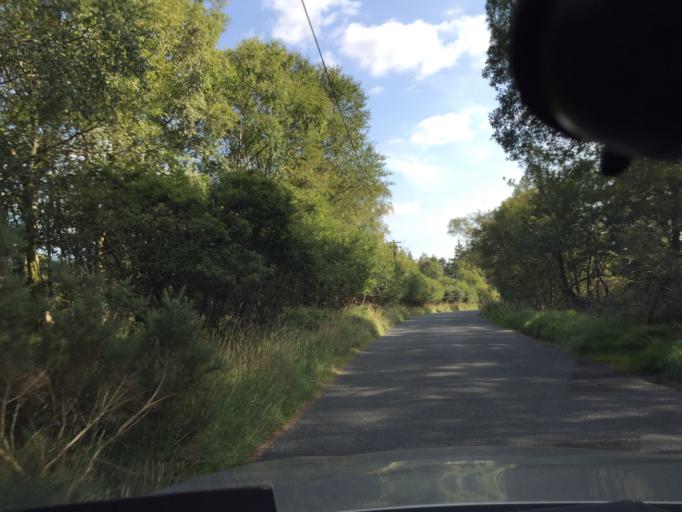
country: IE
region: Leinster
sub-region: Wicklow
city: Rathdrum
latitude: 53.0188
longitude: -6.3032
